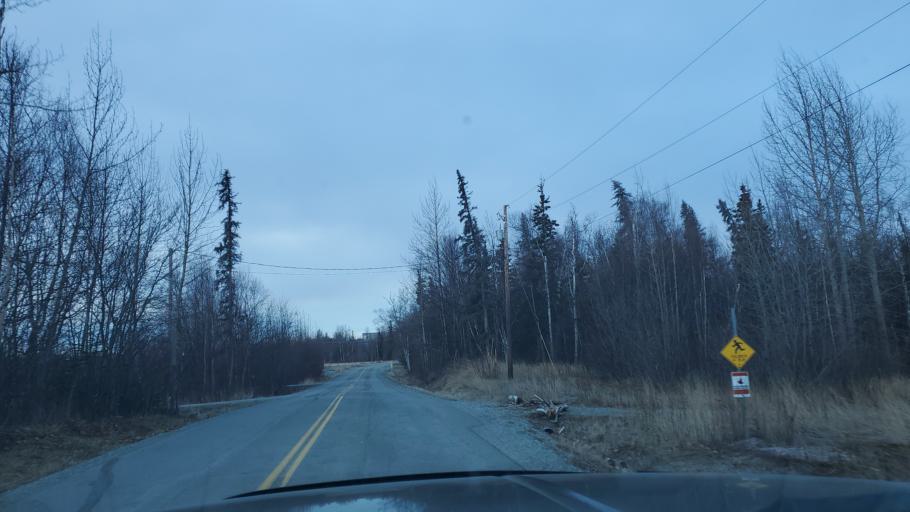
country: US
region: Alaska
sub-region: Matanuska-Susitna Borough
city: Lakes
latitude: 61.5731
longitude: -149.3397
